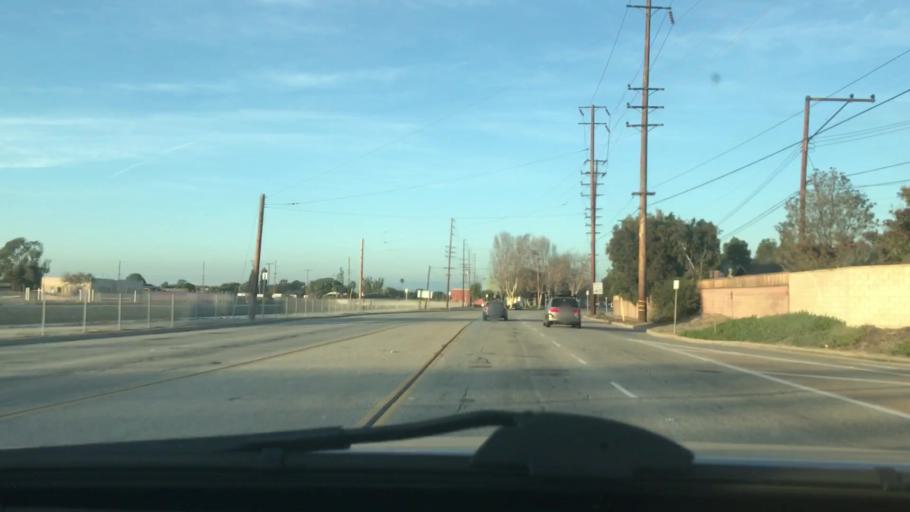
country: US
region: California
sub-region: Orange County
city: Rossmoor
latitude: 33.7779
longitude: -118.1032
